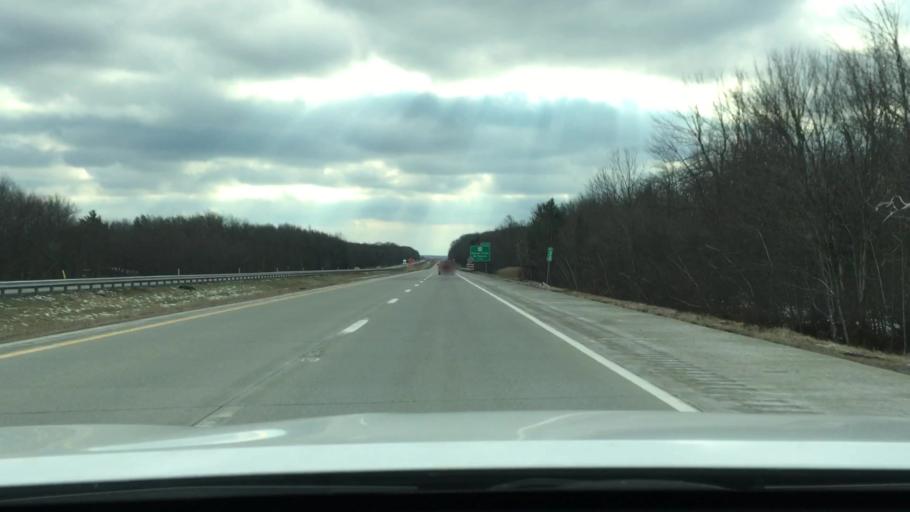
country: US
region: Pennsylvania
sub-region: Monroe County
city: Mount Pocono
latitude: 41.1248
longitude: -75.4002
